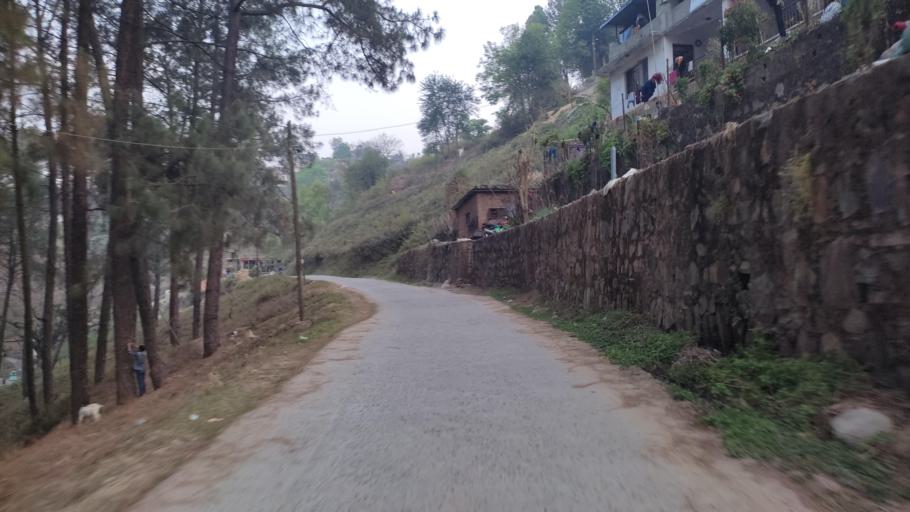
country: NP
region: Central Region
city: Kirtipur
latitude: 27.6693
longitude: 85.2897
